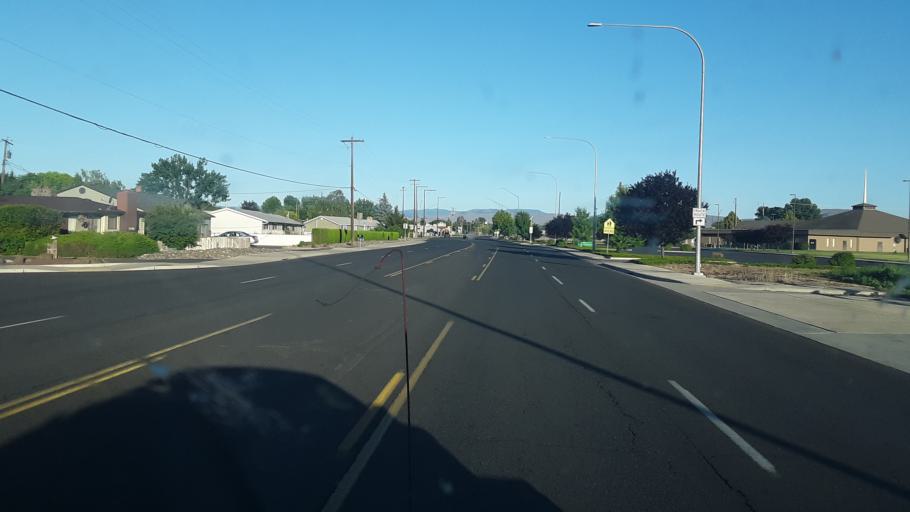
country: US
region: Washington
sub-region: Yakima County
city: West Valley
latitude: 46.5858
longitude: -120.6009
